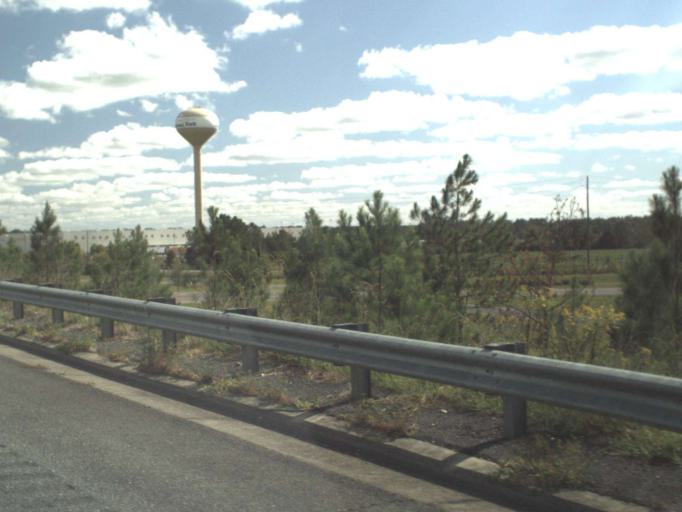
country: US
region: Florida
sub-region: Jackson County
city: Marianna
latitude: 30.7537
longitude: -85.2741
